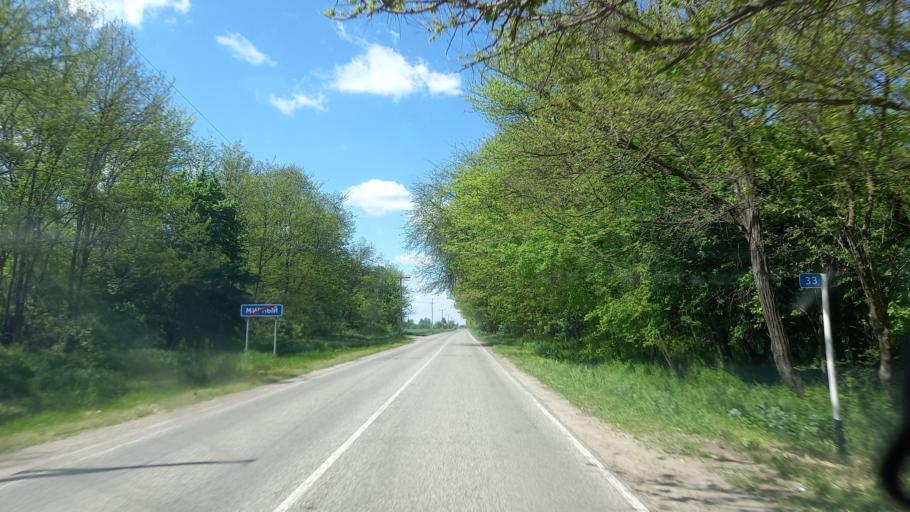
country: RU
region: Krasnodarskiy
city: Tbilisskaya
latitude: 45.3380
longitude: 40.3118
